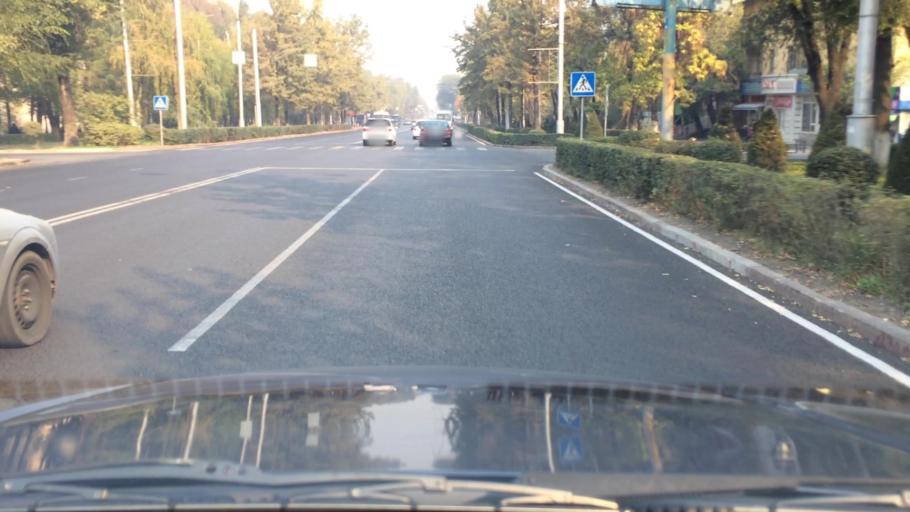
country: KG
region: Chuy
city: Bishkek
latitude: 42.8462
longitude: 74.5863
